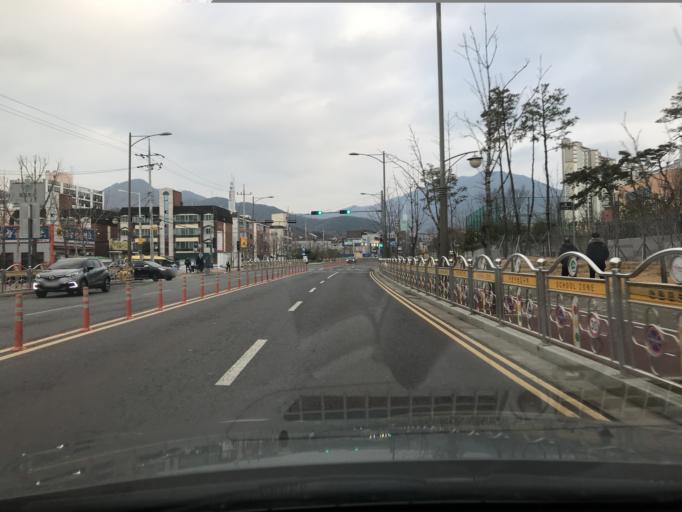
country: KR
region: Daegu
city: Hwawon
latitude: 35.6944
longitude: 128.4507
